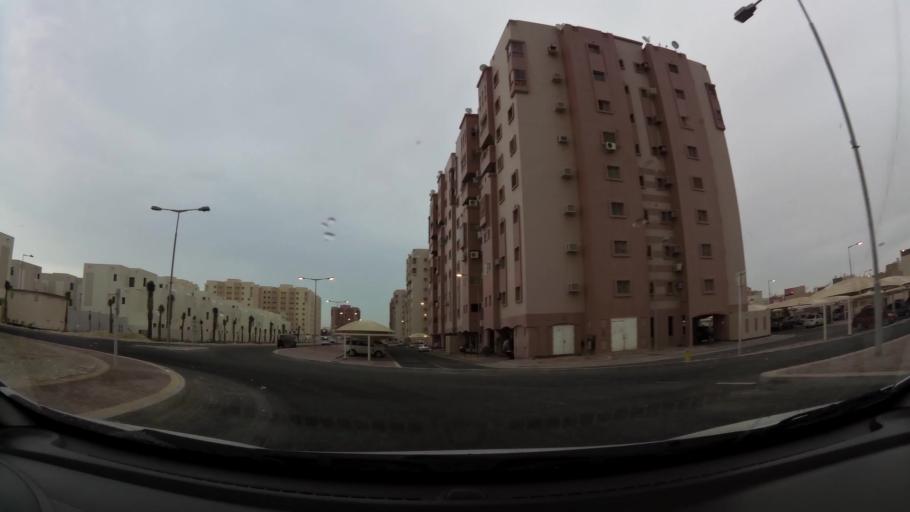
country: BH
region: Central Governorate
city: Madinat Hamad
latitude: 26.1198
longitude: 50.4853
